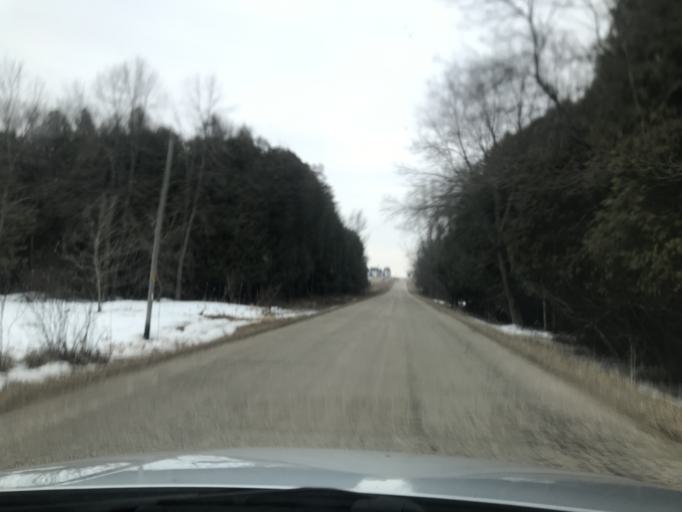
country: US
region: Wisconsin
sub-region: Marinette County
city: Peshtigo
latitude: 45.1044
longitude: -87.9322
